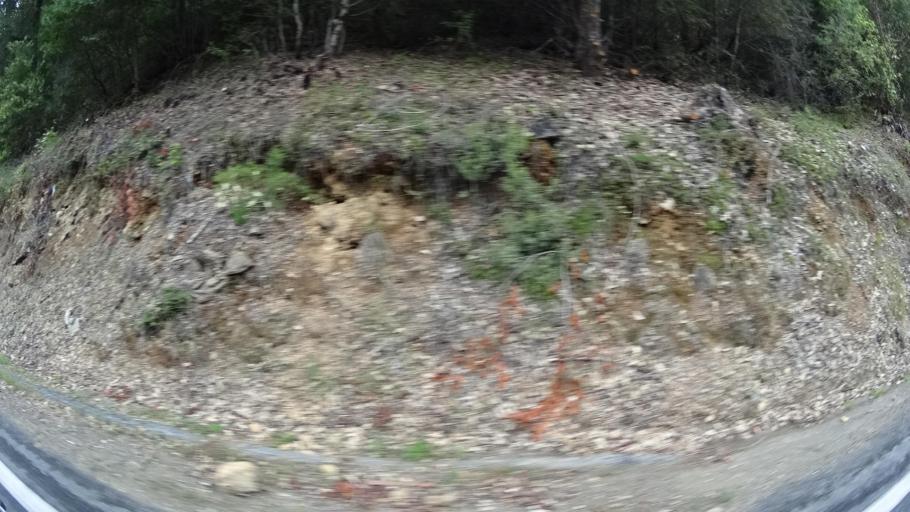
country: US
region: California
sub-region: Humboldt County
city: Willow Creek
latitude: 41.2598
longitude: -123.6154
